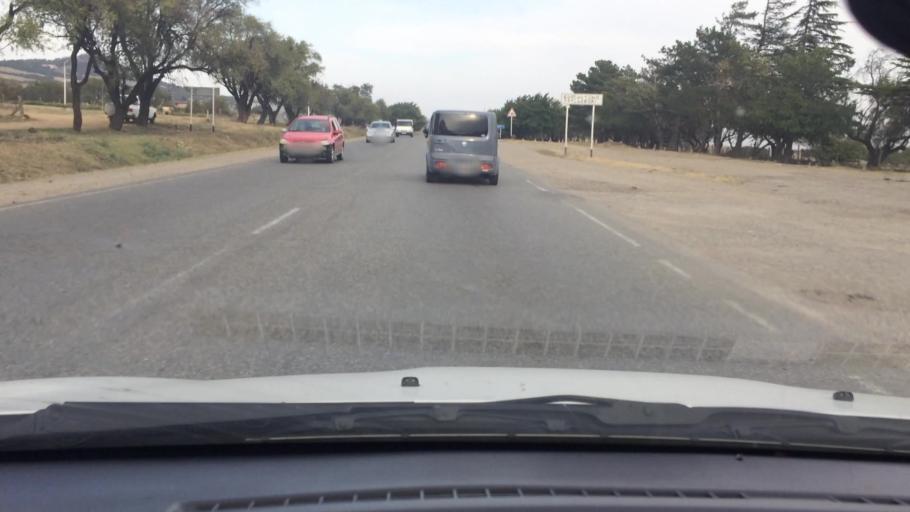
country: GE
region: T'bilisi
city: Tbilisi
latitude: 41.6344
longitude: 44.8198
